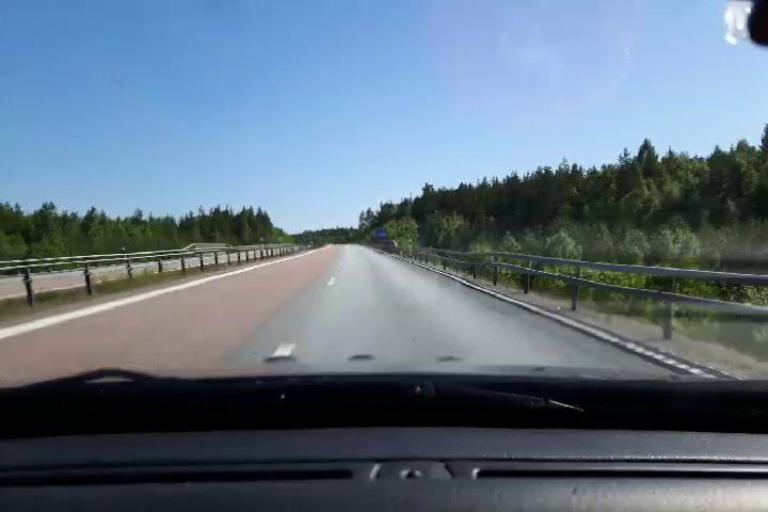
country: SE
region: Gaevleborg
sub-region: Soderhamns Kommun
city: Soderhamn
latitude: 61.4215
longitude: 16.9852
